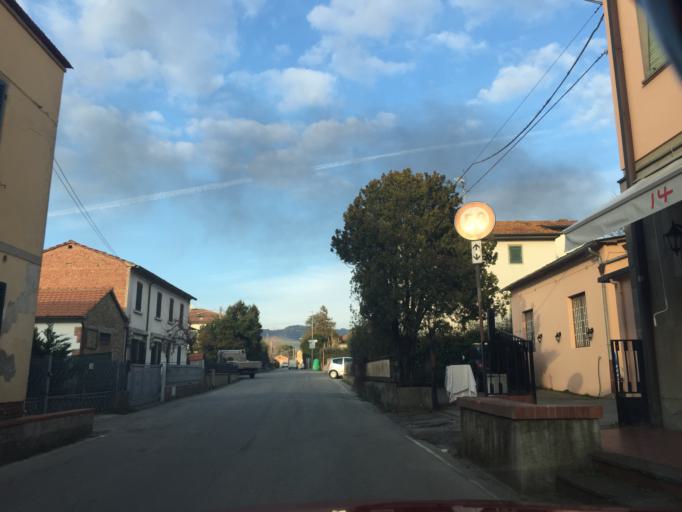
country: IT
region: Tuscany
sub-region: Provincia di Pistoia
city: San Rocco
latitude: 43.8286
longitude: 10.8628
